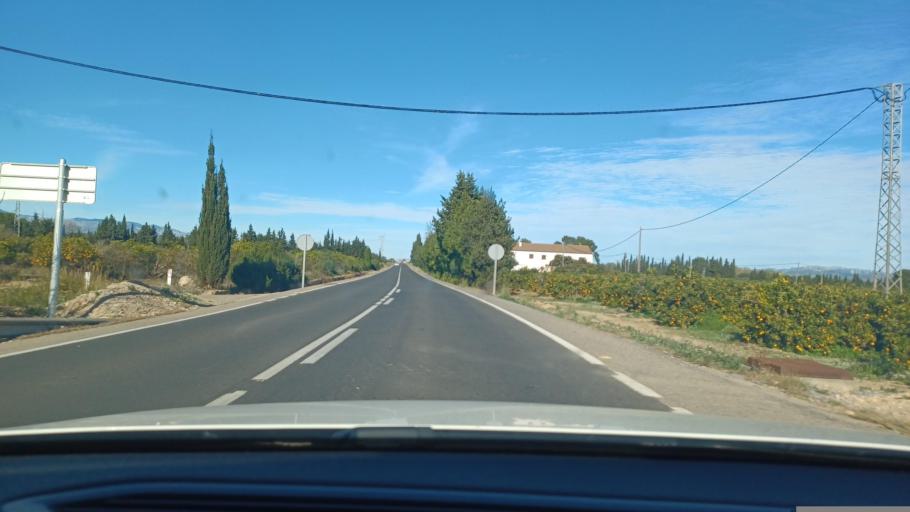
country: ES
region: Catalonia
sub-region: Provincia de Tarragona
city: Santa Barbara
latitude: 40.6985
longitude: 0.5049
